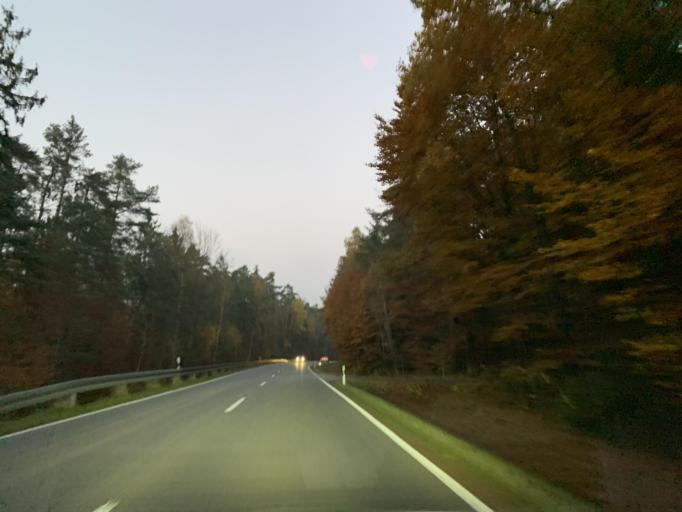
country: DE
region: Bavaria
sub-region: Upper Palatinate
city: Brunn
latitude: 49.2265
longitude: 12.1557
